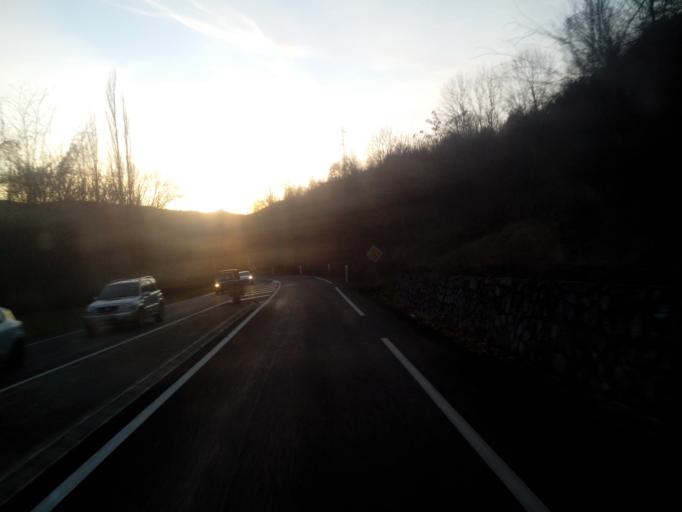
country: FR
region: Midi-Pyrenees
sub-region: Departement de l'Ariege
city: Saint-Paul-de-Jarrat
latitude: 42.9176
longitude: 1.6842
